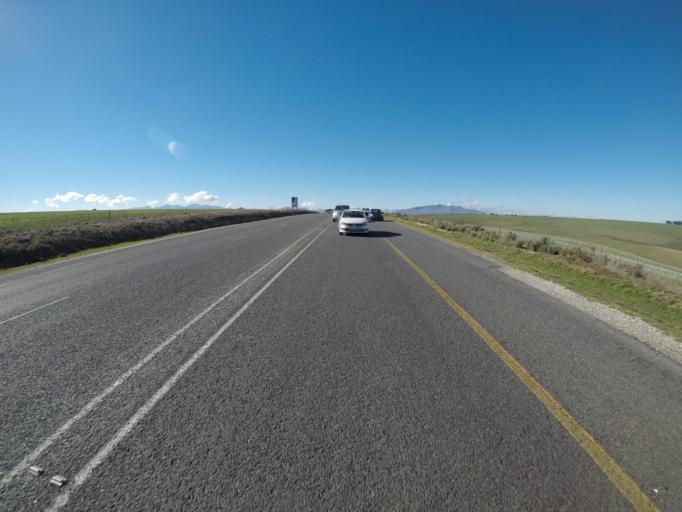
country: ZA
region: Western Cape
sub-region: Overberg District Municipality
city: Caledon
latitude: -34.2246
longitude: 19.2765
